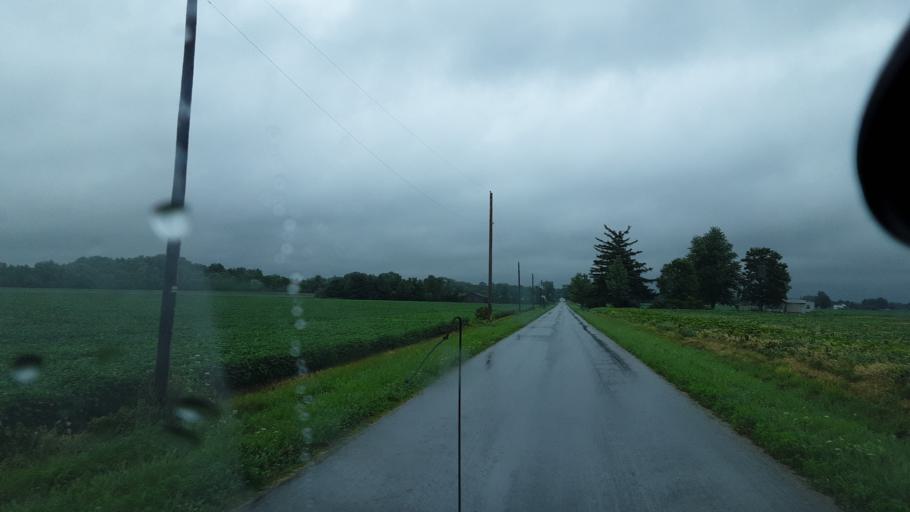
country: US
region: Indiana
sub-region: Adams County
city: Decatur
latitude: 40.7755
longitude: -84.8547
